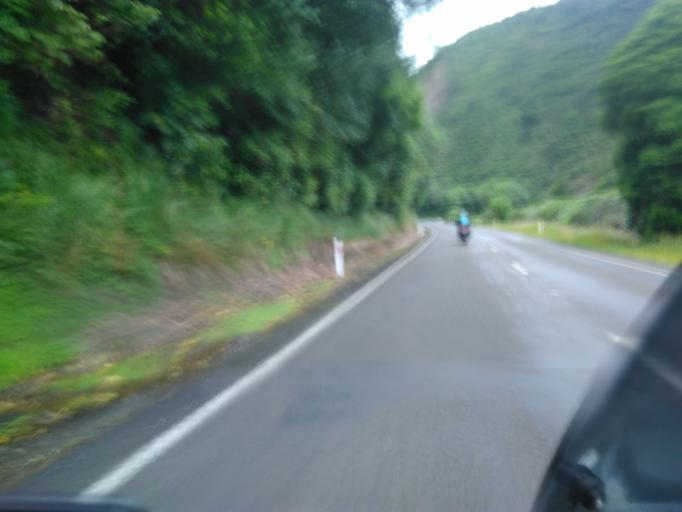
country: NZ
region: Bay of Plenty
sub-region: Opotiki District
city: Opotiki
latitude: -38.2989
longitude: 177.3932
